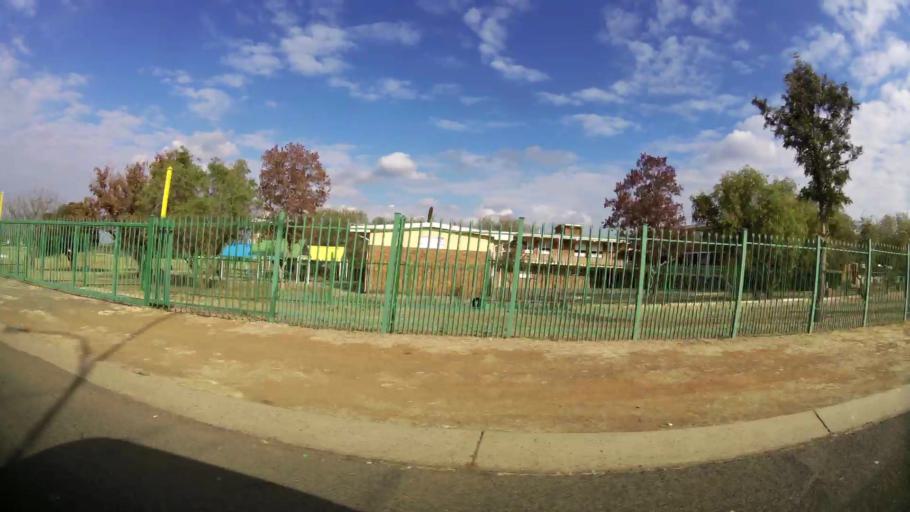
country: ZA
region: Orange Free State
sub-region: Mangaung Metropolitan Municipality
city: Bloemfontein
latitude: -29.0754
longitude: 26.2323
